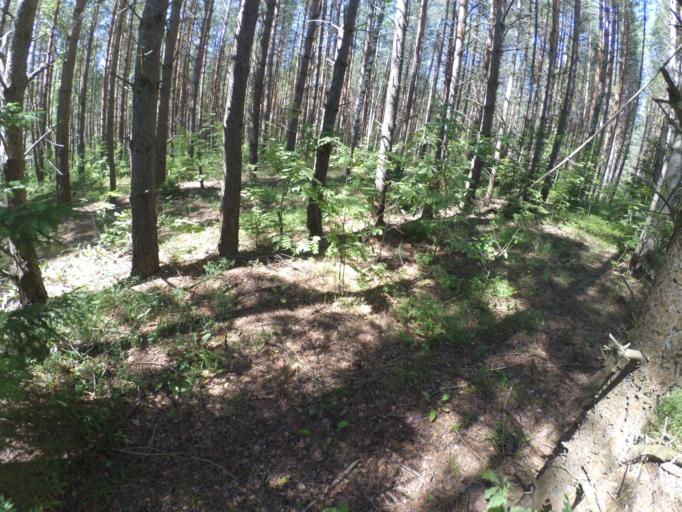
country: RU
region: Moskovskaya
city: Fosforitnyy
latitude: 55.3383
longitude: 38.9303
